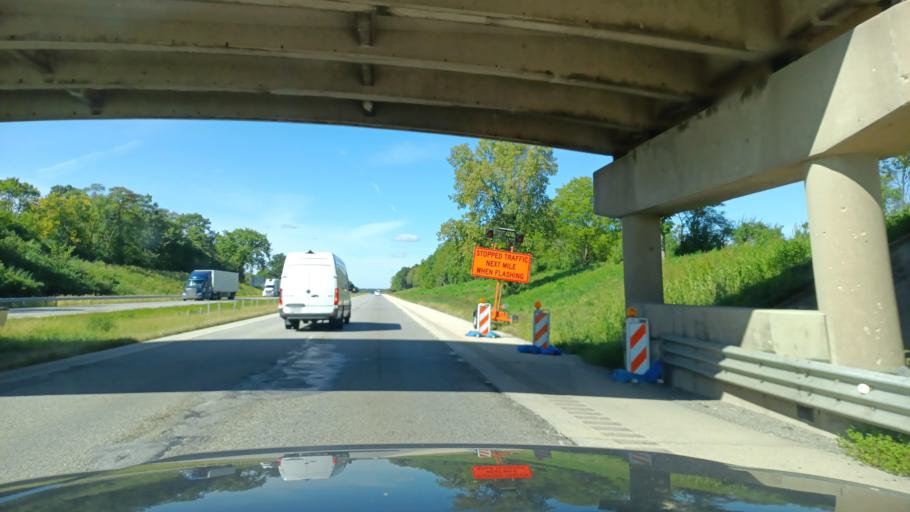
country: US
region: Illinois
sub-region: Vermilion County
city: Danville
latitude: 40.1160
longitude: -87.5635
